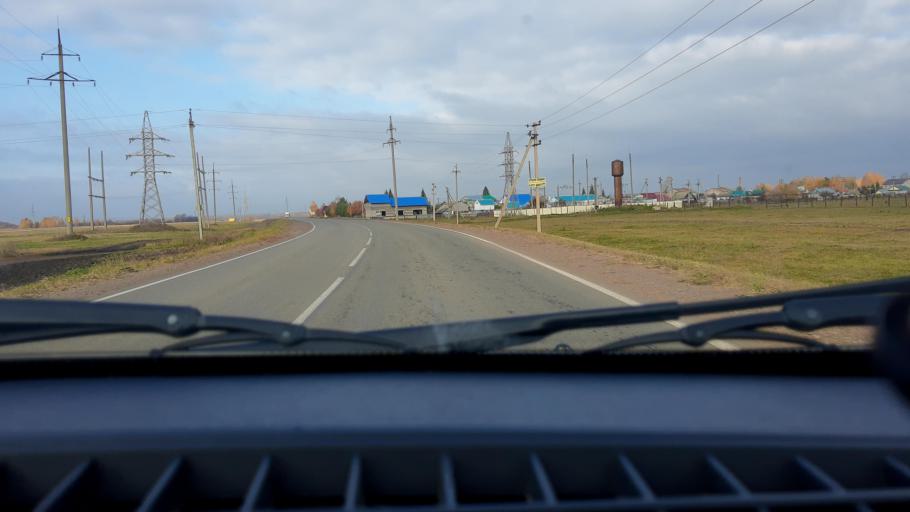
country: RU
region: Bashkortostan
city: Kabakovo
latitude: 54.5459
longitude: 56.0415
